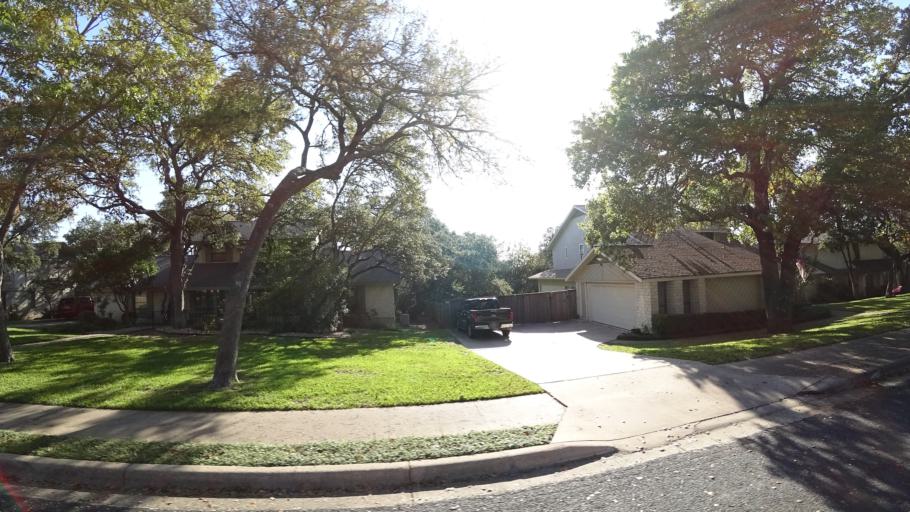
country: US
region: Texas
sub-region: Williamson County
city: Anderson Mill
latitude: 30.4425
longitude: -97.8110
